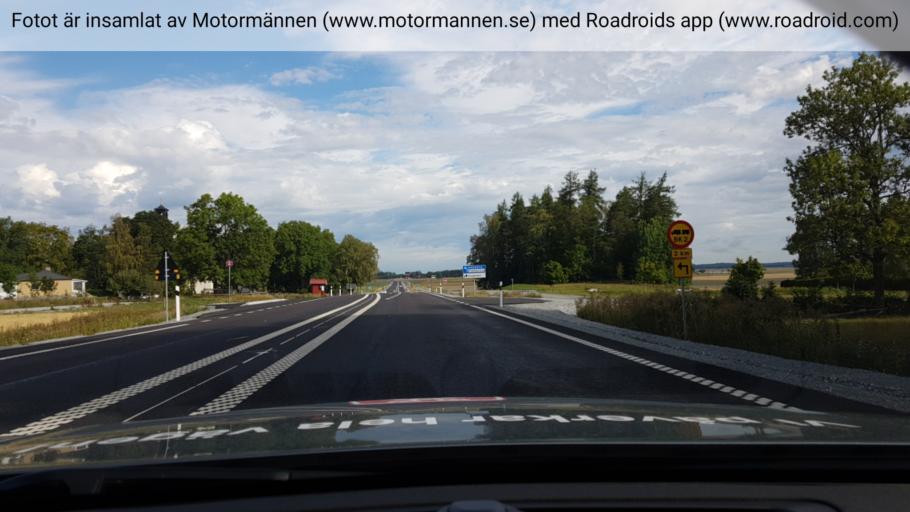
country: SE
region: Uppsala
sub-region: Enkopings Kommun
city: Irsta
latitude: 59.7366
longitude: 16.9543
